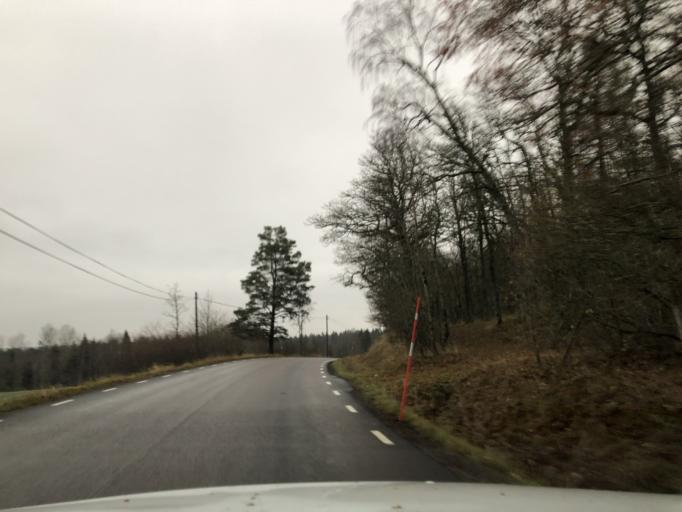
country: SE
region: Vaestra Goetaland
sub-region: Ulricehamns Kommun
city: Ulricehamn
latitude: 57.8515
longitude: 13.3893
